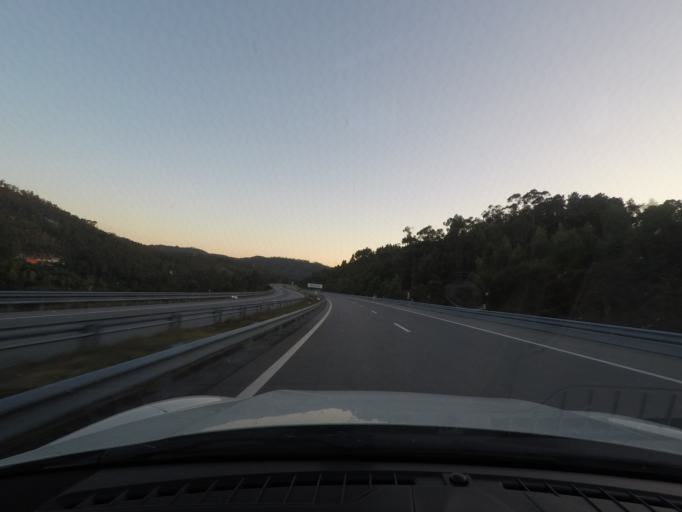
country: PT
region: Braga
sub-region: Guimaraes
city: Serzedo
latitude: 41.4149
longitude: -8.2040
